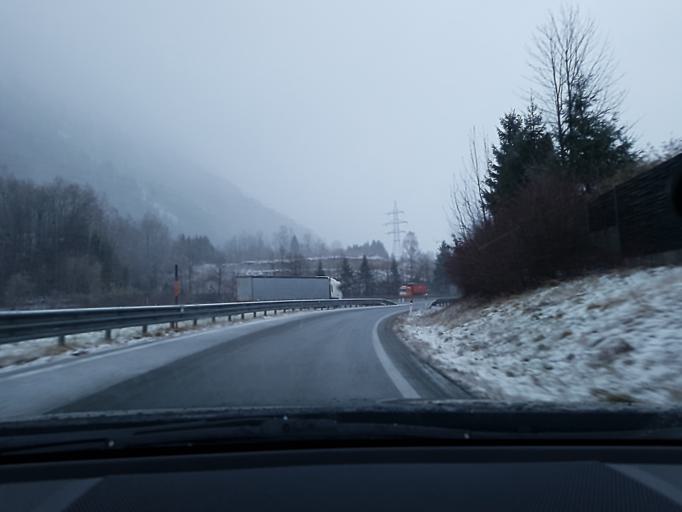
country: AT
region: Salzburg
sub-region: Politischer Bezirk Hallein
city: Golling an der Salzach
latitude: 47.5929
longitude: 13.1531
